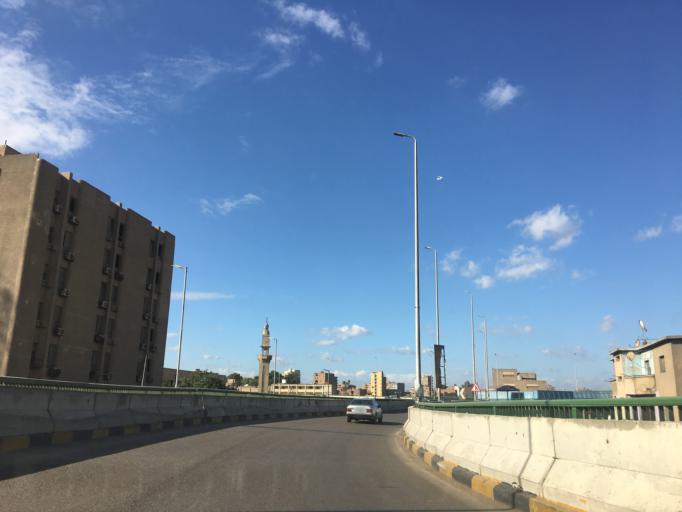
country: EG
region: Al Jizah
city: Al Jizah
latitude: 30.0276
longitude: 31.2004
